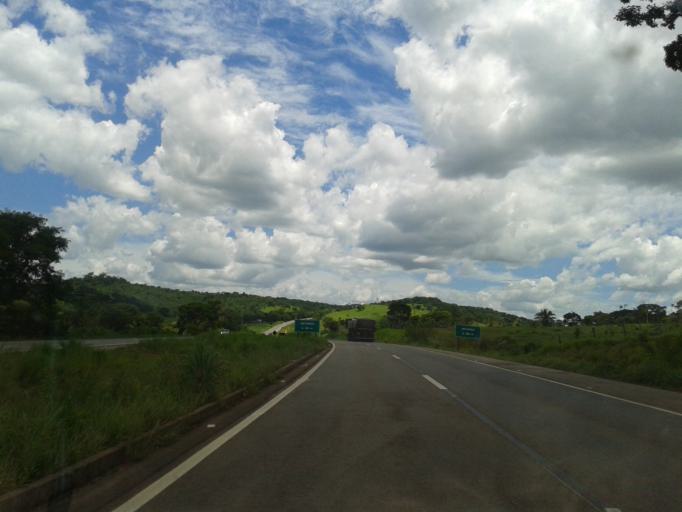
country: BR
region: Goias
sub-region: Neropolis
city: Neropolis
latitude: -16.3483
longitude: -49.2568
